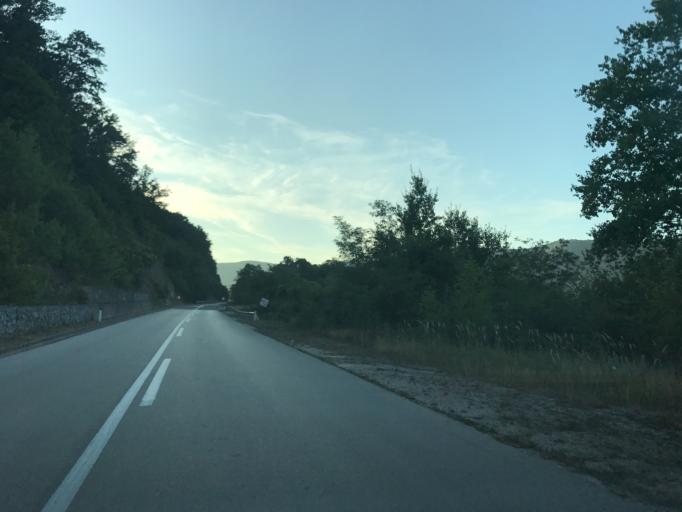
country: RO
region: Caras-Severin
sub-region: Comuna Berzasca
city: Berzasca
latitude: 44.6262
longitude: 21.9920
